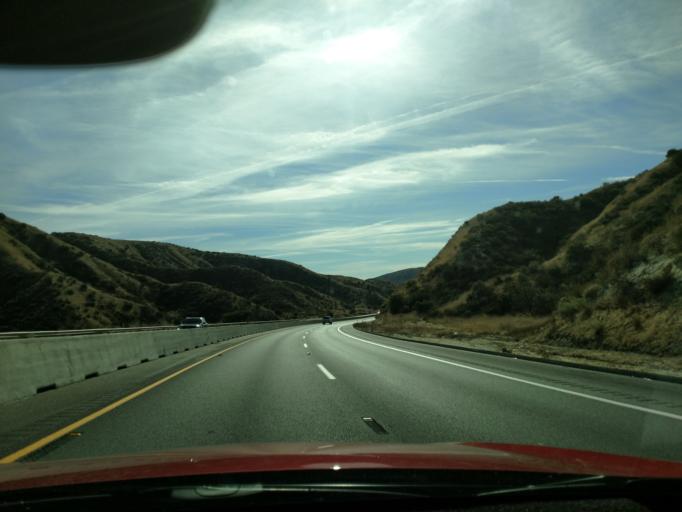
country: US
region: California
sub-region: Riverside County
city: Beaumont
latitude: 33.8951
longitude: -116.9875
